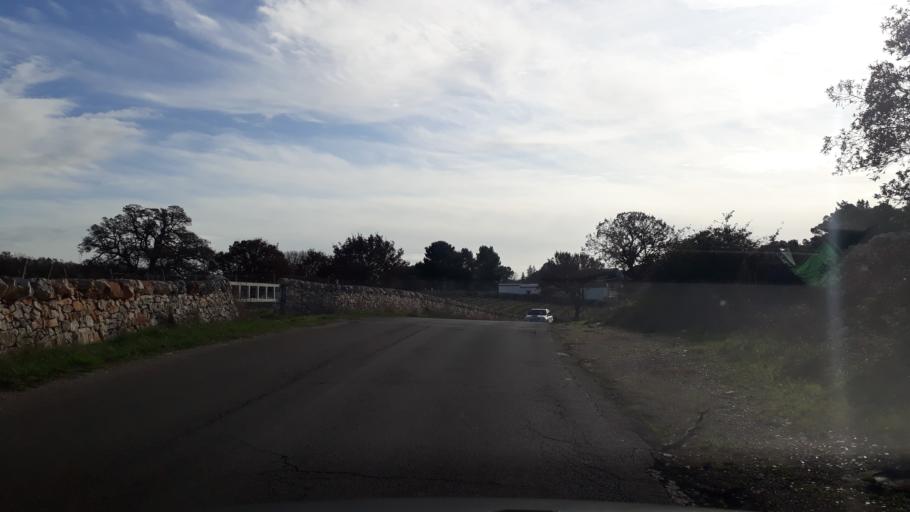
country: IT
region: Apulia
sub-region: Provincia di Taranto
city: Martina Franca
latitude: 40.6756
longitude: 17.3619
